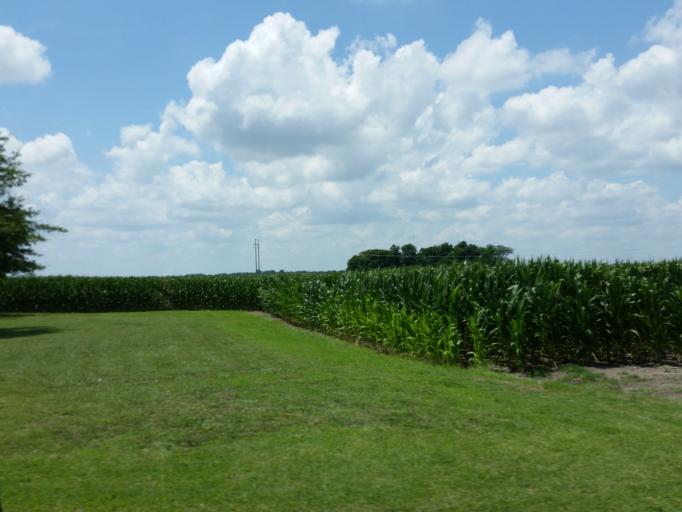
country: US
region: Tennessee
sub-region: Lake County
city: Ridgely
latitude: 36.2067
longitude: -89.4618
